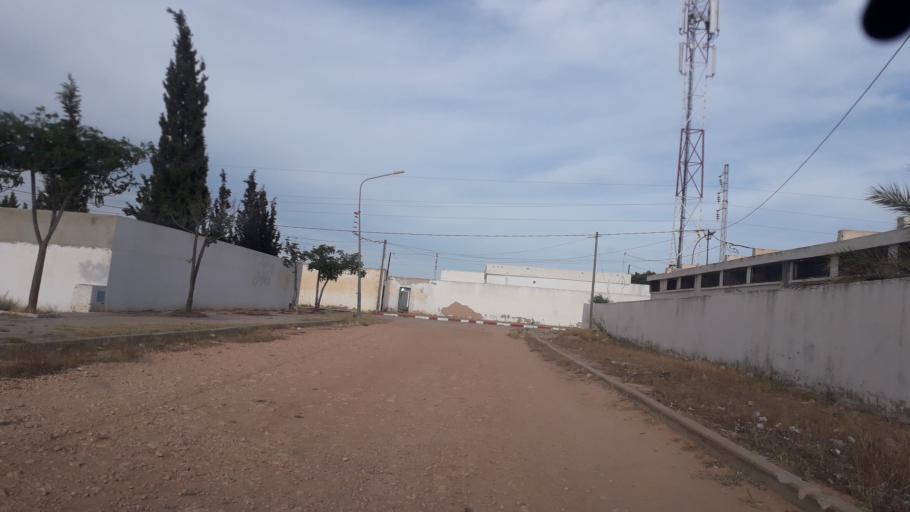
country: TN
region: Safaqis
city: Al Qarmadah
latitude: 34.8879
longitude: 10.7606
